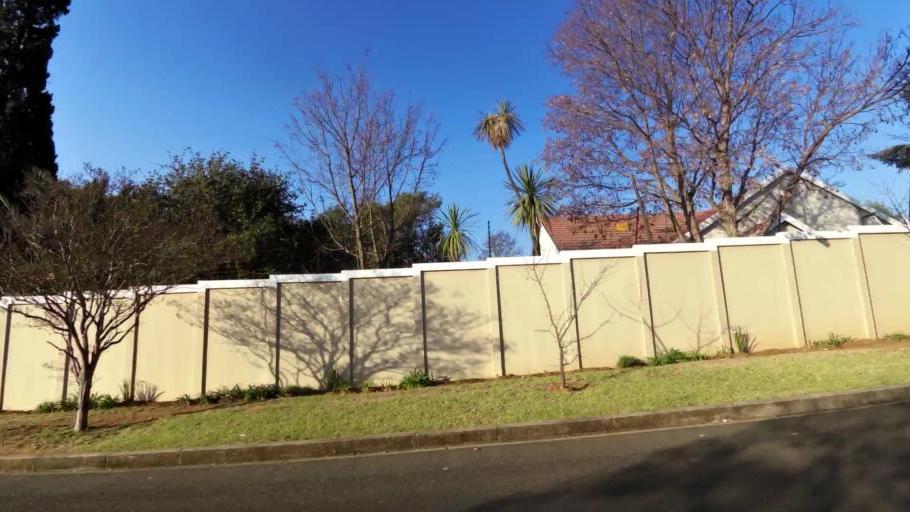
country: ZA
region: Gauteng
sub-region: City of Johannesburg Metropolitan Municipality
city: Johannesburg
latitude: -26.1572
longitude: 27.9910
